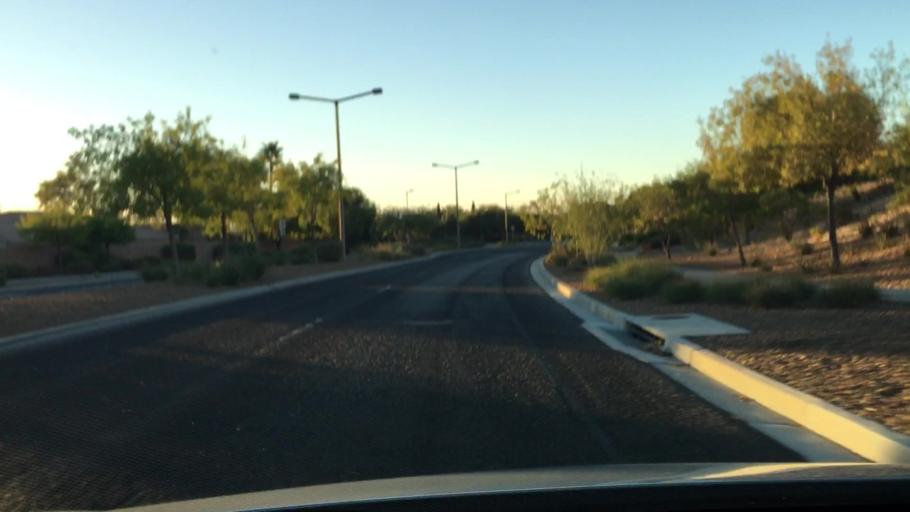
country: US
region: Nevada
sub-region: Clark County
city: Summerlin South
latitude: 36.1242
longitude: -115.3371
